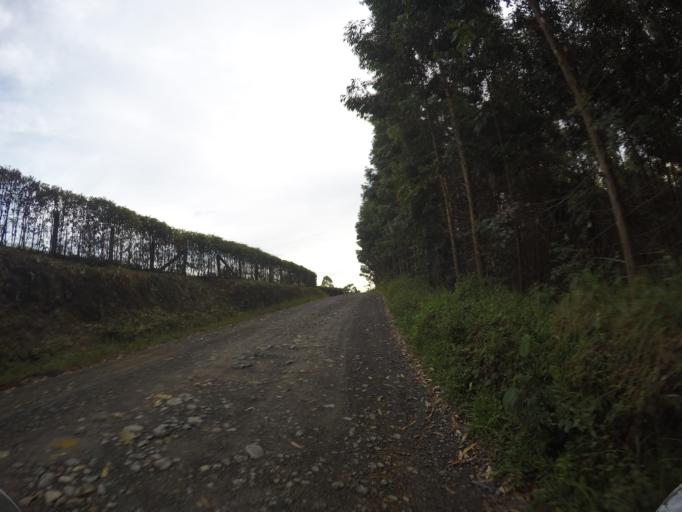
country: CO
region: Quindio
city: Filandia
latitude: 4.7138
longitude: -75.6293
